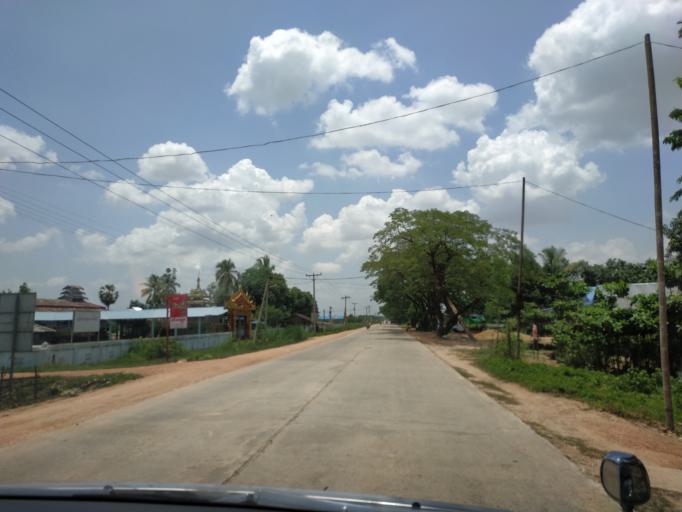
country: MM
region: Bago
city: Bago
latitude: 17.4797
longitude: 96.4880
